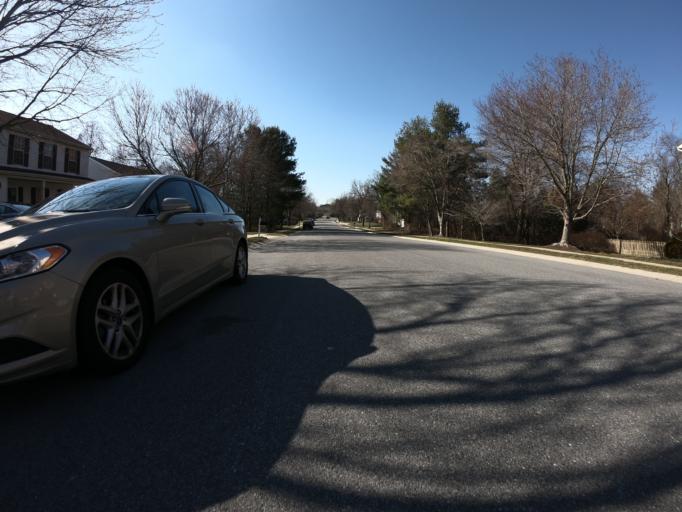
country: US
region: Maryland
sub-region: Howard County
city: Ellicott City
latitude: 39.2455
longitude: -76.8110
